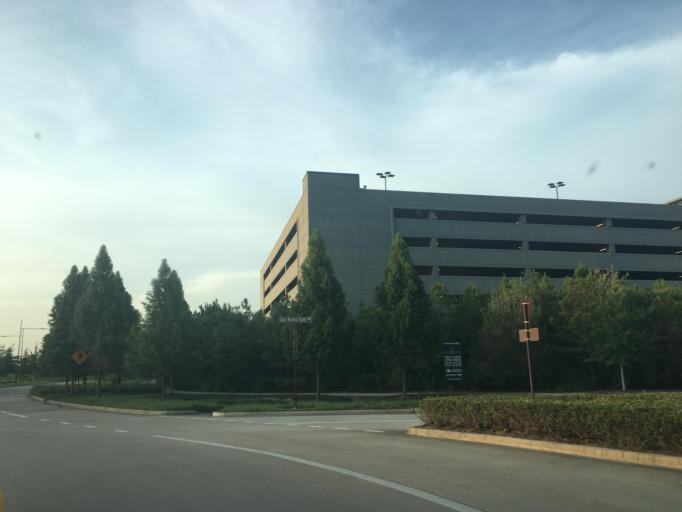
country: US
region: Texas
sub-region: Harris County
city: Spring
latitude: 30.0972
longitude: -95.4382
